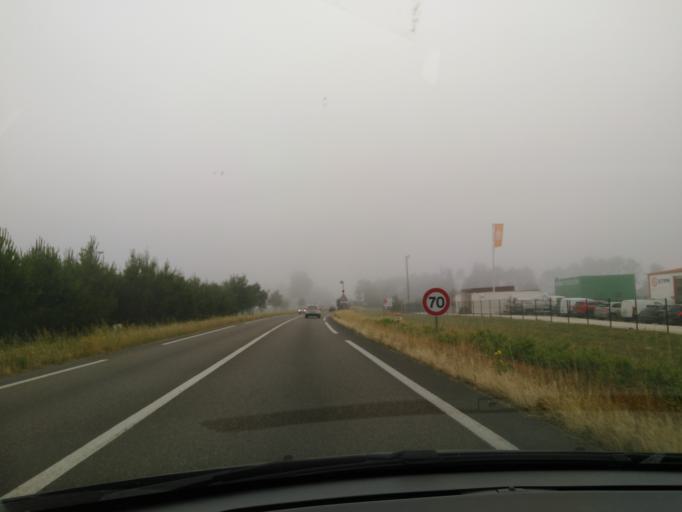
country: FR
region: Aquitaine
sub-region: Departement des Landes
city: Begaar
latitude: 43.8278
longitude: -0.8300
